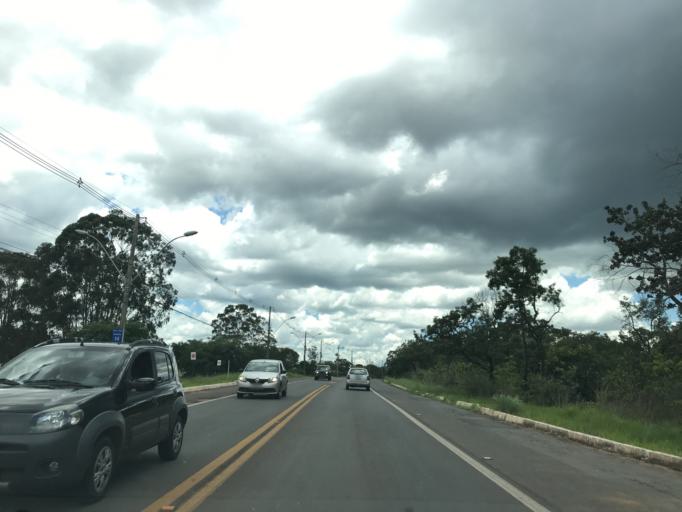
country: BR
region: Federal District
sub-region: Brasilia
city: Brasilia
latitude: -15.8840
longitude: -47.9576
